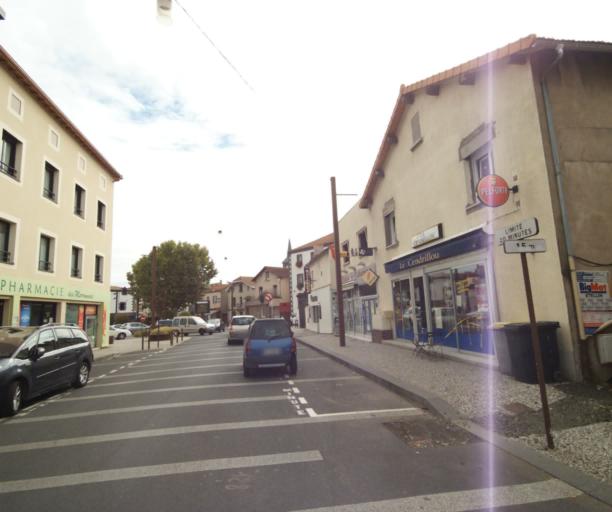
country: FR
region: Auvergne
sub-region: Departement du Puy-de-Dome
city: Le Cendre
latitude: 45.7218
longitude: 3.1867
